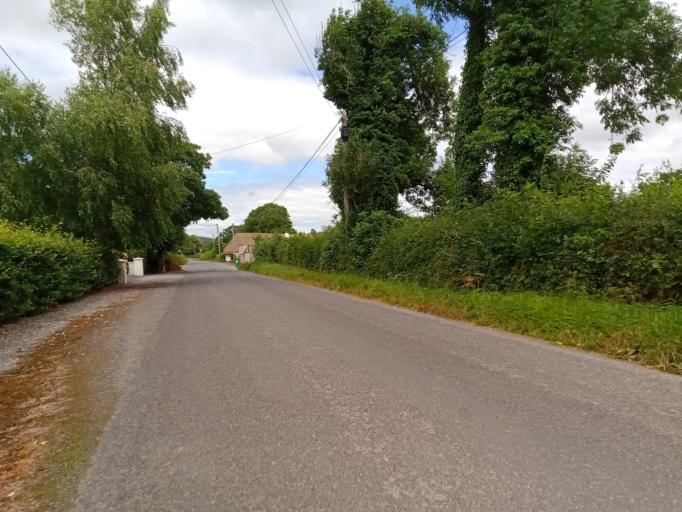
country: IE
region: Leinster
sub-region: Kilkenny
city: Callan
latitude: 52.5771
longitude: -7.3788
